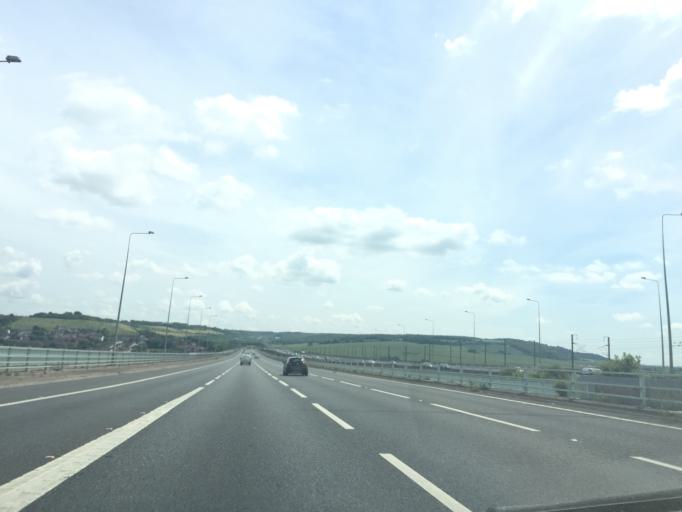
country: GB
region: England
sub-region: Medway
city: Cuxton
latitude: 51.3811
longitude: 0.4711
